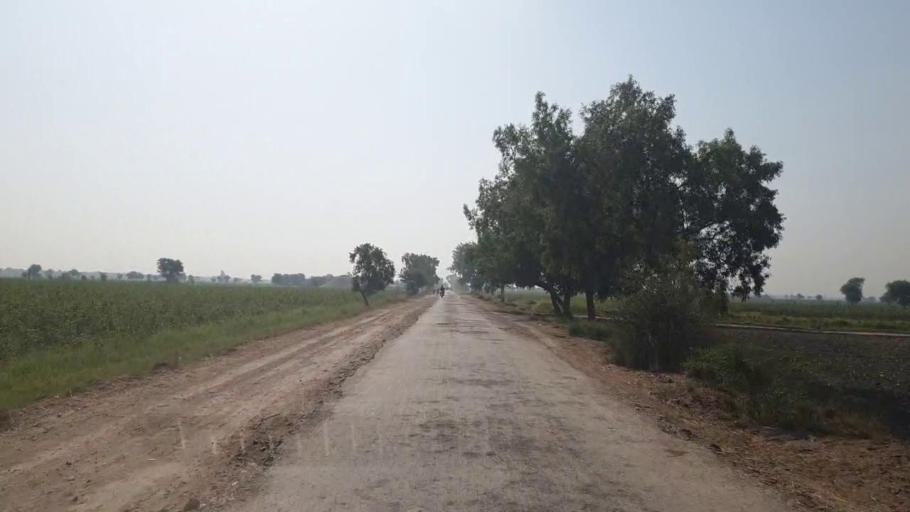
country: PK
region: Sindh
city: Shahdadpur
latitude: 25.9331
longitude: 68.7301
